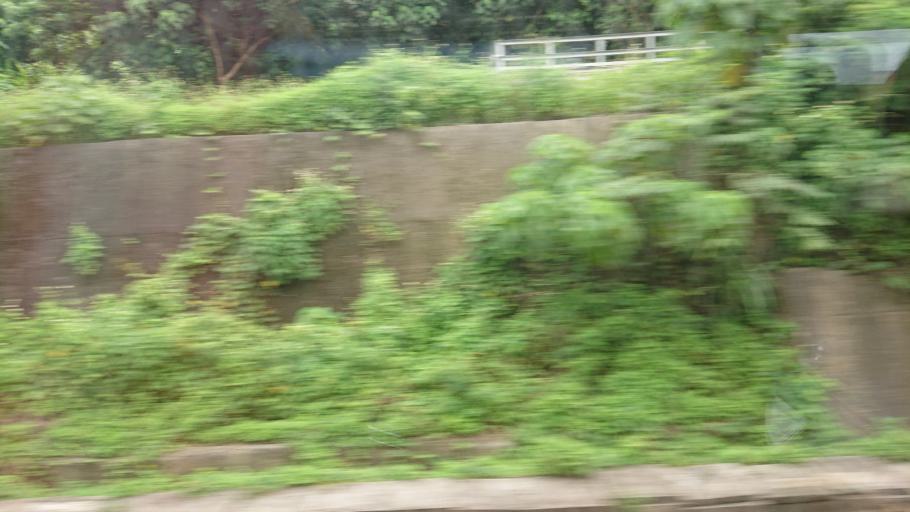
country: TW
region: Taiwan
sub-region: Yilan
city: Yilan
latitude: 24.9152
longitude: 121.8795
